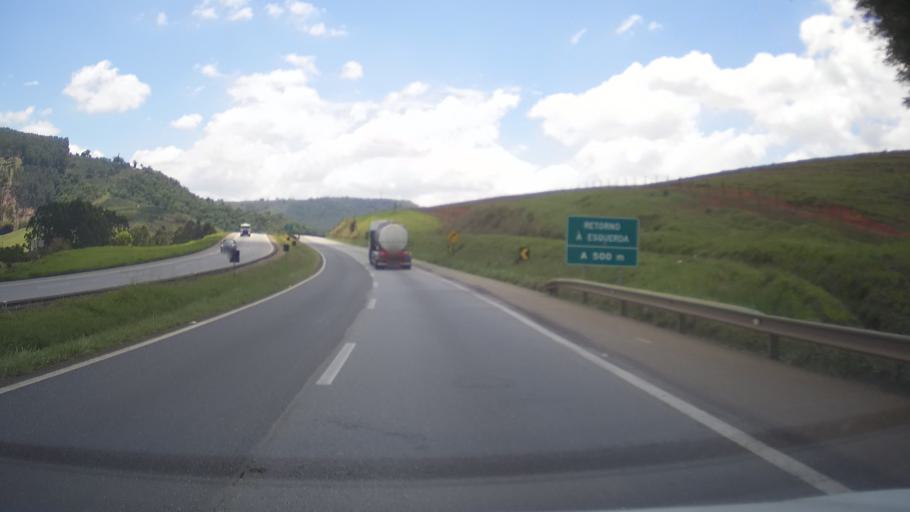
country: BR
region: Minas Gerais
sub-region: Campanha
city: Campanha
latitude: -21.8130
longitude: -45.4904
